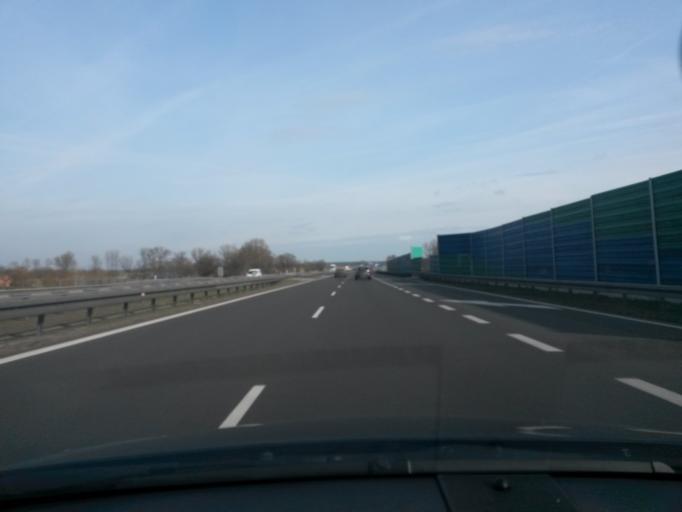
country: PL
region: Greater Poland Voivodeship
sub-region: Powiat koninski
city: Rzgow Pierwszy
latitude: 52.2036
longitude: 18.0262
